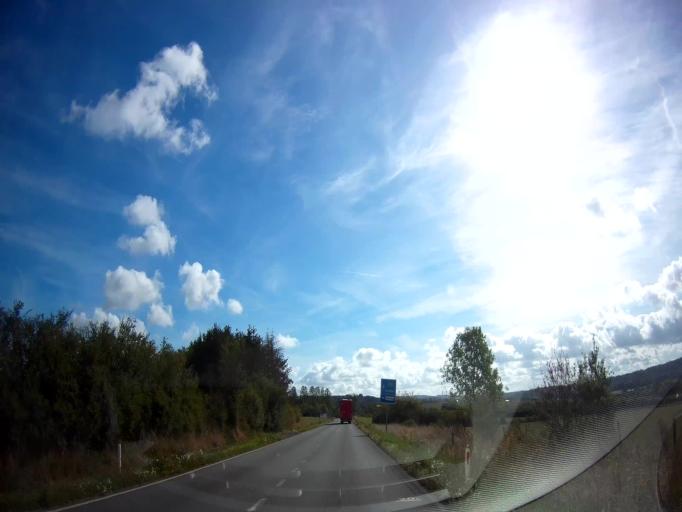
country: BE
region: Wallonia
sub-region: Province de Namur
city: Rochefort
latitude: 50.1673
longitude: 5.1914
